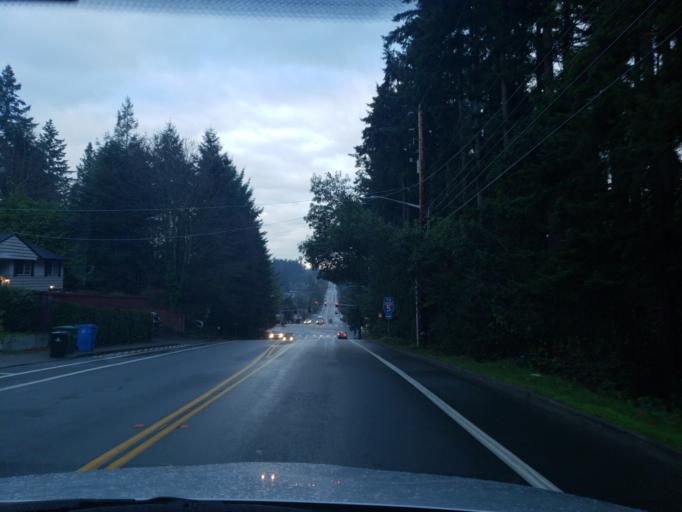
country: US
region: Washington
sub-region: King County
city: Shoreline
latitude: 47.7765
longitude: -122.3353
